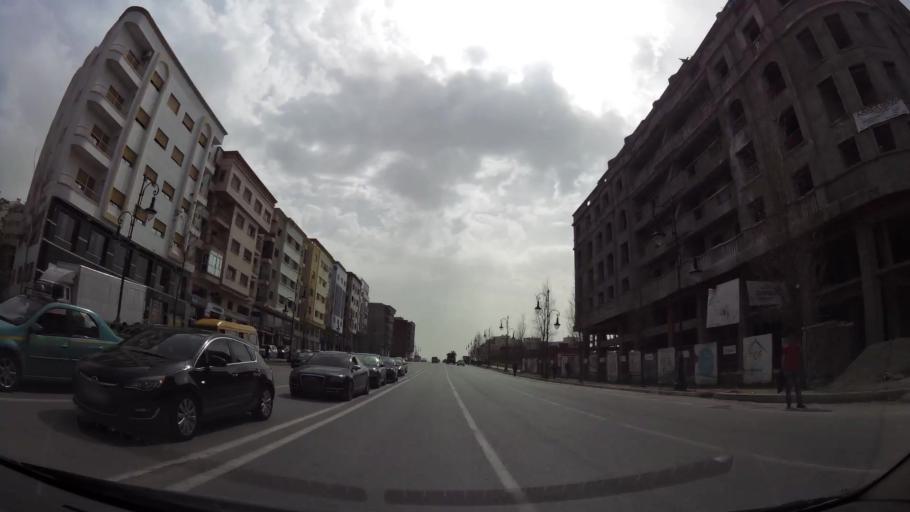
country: MA
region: Tanger-Tetouan
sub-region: Tanger-Assilah
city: Tangier
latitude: 35.7623
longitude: -5.8392
